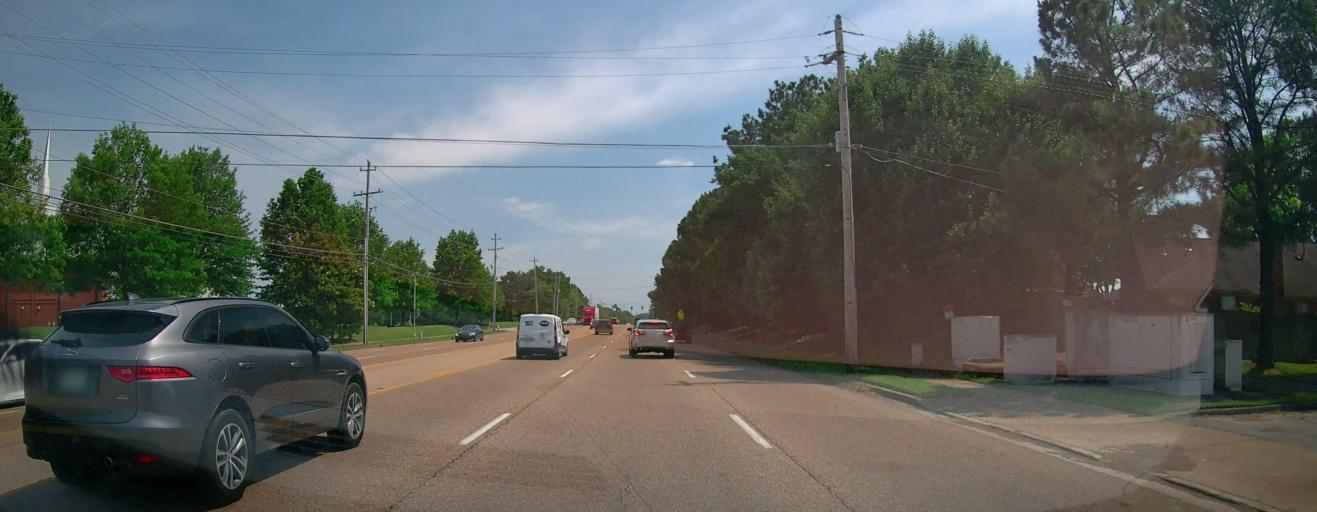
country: US
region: Tennessee
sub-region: Shelby County
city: Germantown
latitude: 35.0303
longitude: -89.7959
